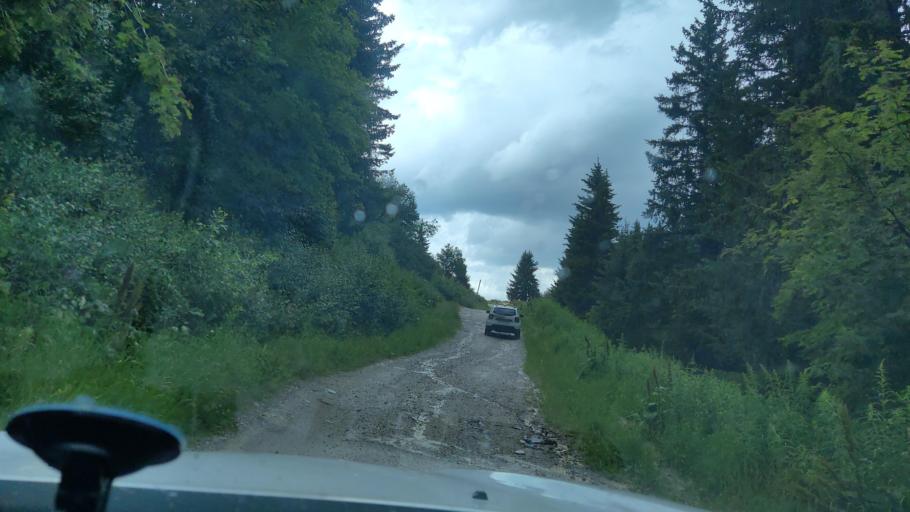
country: FR
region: Rhone-Alpes
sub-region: Departement de la Savoie
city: Courchevel
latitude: 45.3982
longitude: 6.6389
